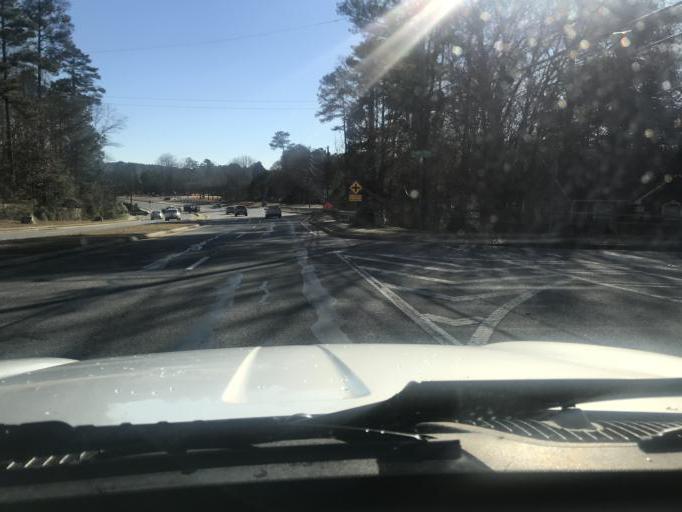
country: US
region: Georgia
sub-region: Gwinnett County
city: Lawrenceville
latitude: 33.9684
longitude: -84.0423
